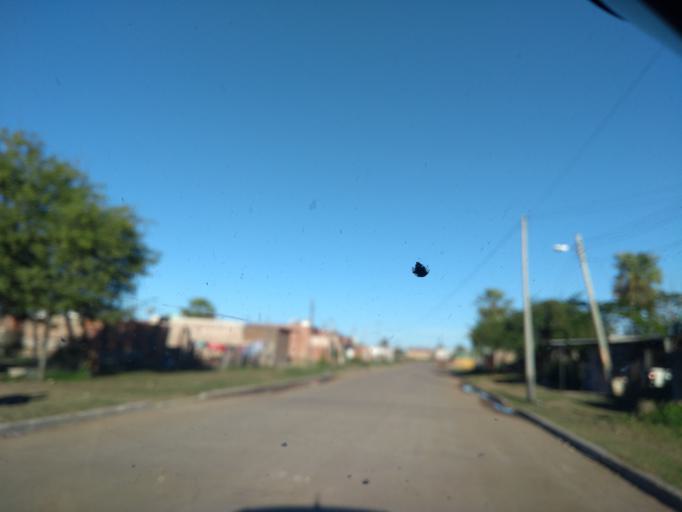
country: AR
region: Chaco
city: Barranqueras
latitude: -27.4916
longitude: -58.9369
